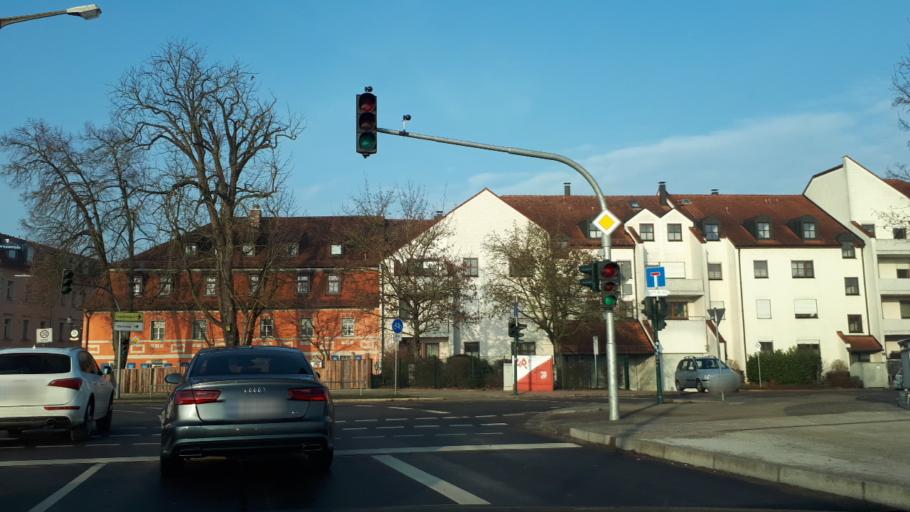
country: DE
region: Bavaria
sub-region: Upper Palatinate
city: Regensburg
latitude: 49.0302
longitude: 12.1019
